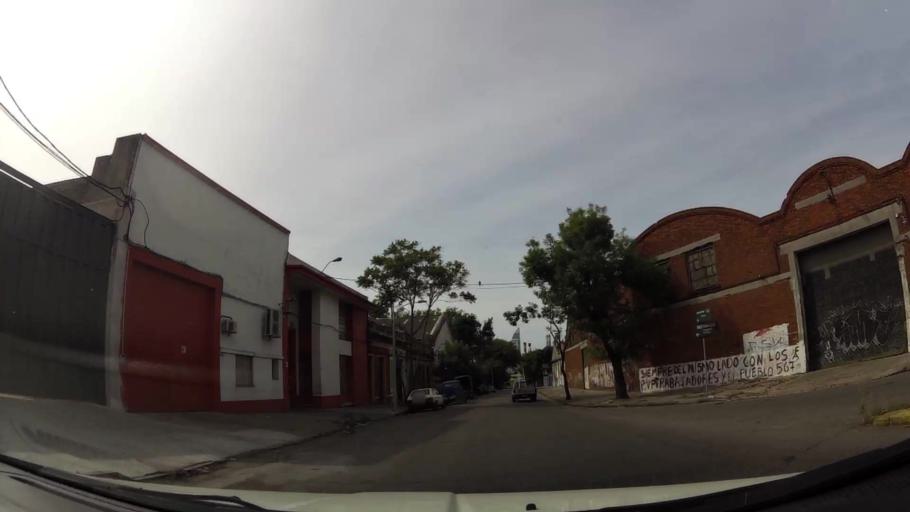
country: UY
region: Montevideo
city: Montevideo
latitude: -34.8794
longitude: -56.1994
